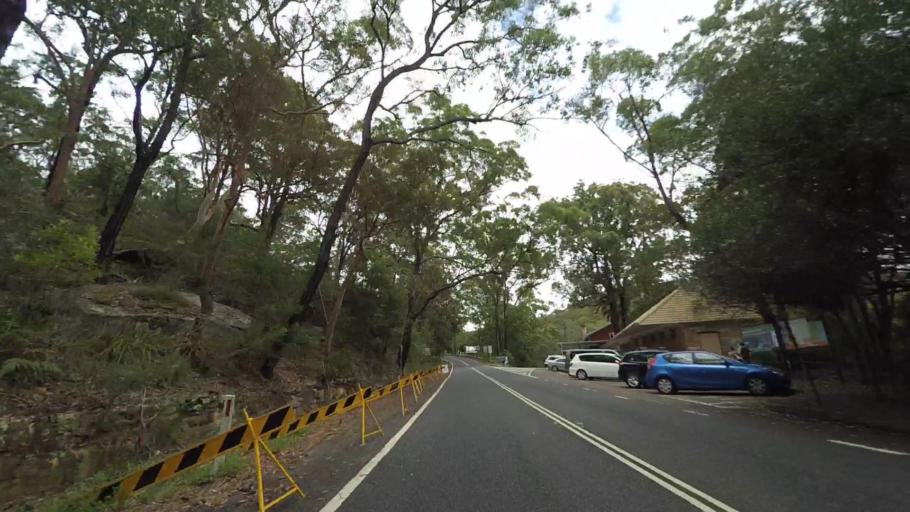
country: AU
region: New South Wales
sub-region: Sutherland Shire
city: Loftus
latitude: -34.0748
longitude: 151.0569
